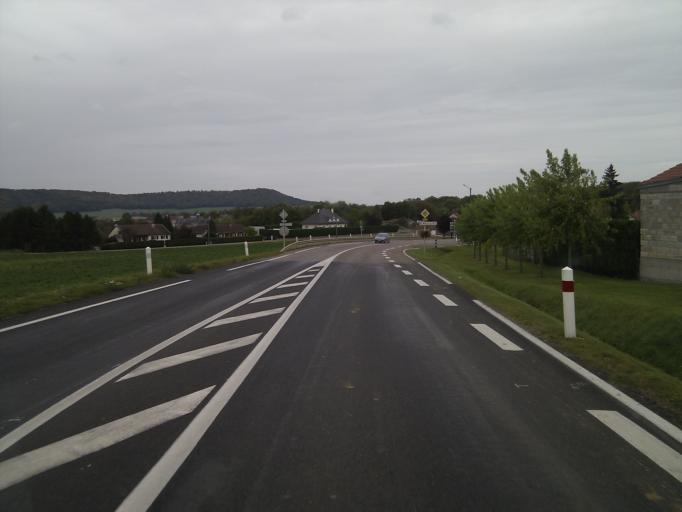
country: FR
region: Champagne-Ardenne
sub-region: Departement de la Haute-Marne
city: Doulaincourt-Saucourt
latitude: 48.2476
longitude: 5.3222
